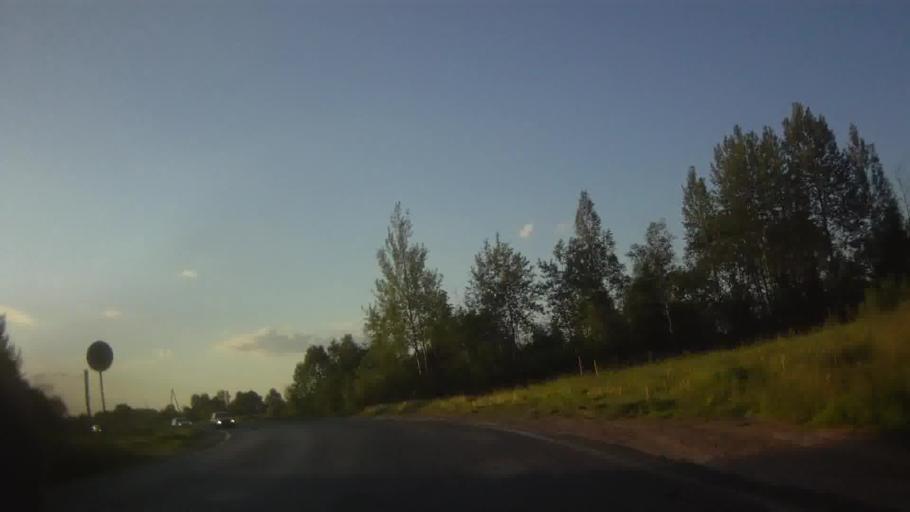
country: LV
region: Salas
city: Sala
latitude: 56.5478
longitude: 25.8009
